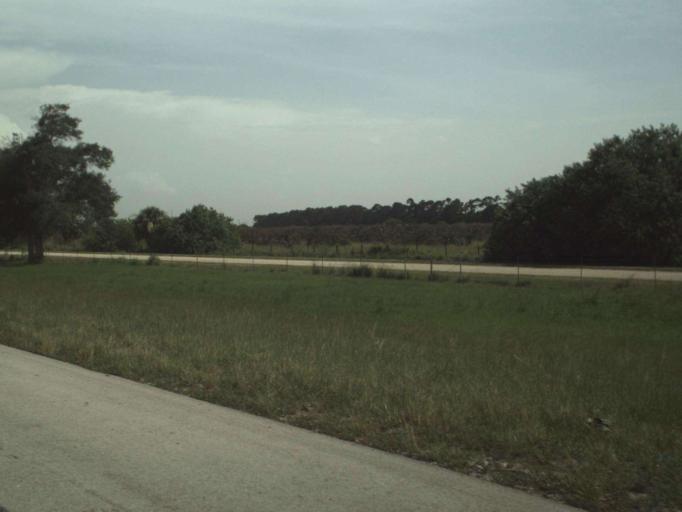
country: US
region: Florida
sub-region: Saint Lucie County
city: Lakewood Park
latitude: 27.5099
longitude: -80.4457
